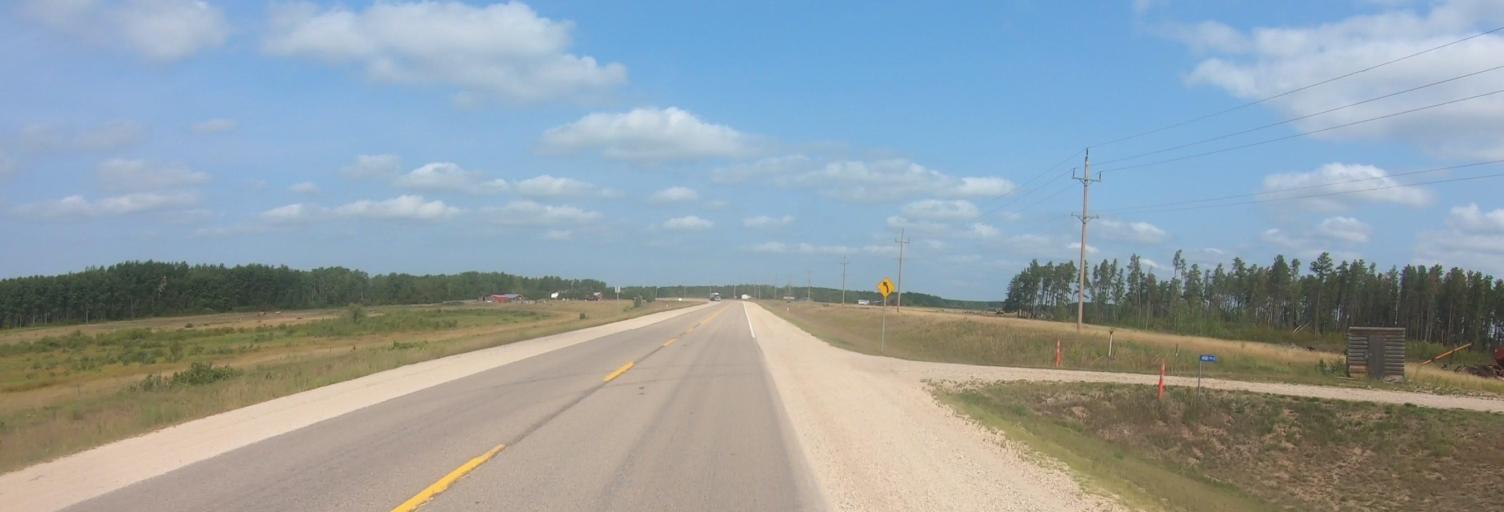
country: CA
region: Manitoba
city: La Broquerie
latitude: 49.2602
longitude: -96.3595
